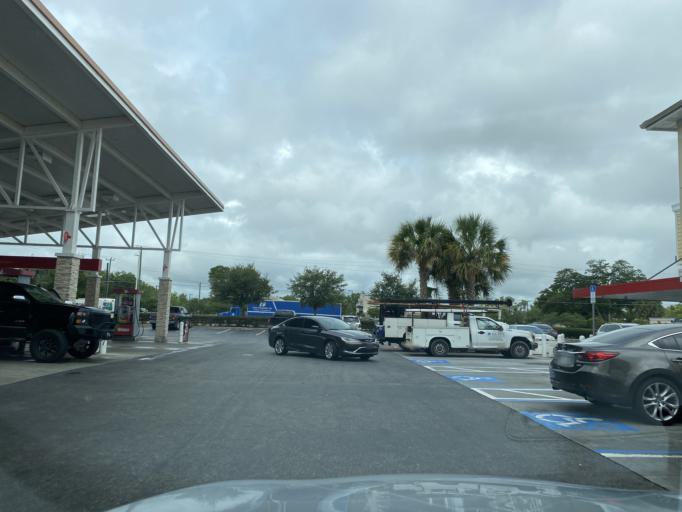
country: US
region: Florida
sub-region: Seminole County
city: Sanford
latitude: 28.7870
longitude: -81.2969
